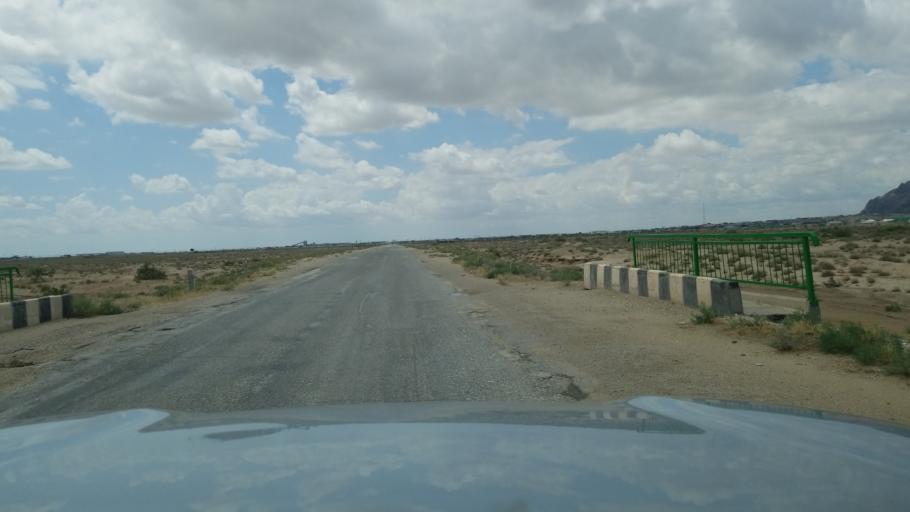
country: TM
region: Balkan
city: Balkanabat
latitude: 39.4867
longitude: 54.4171
